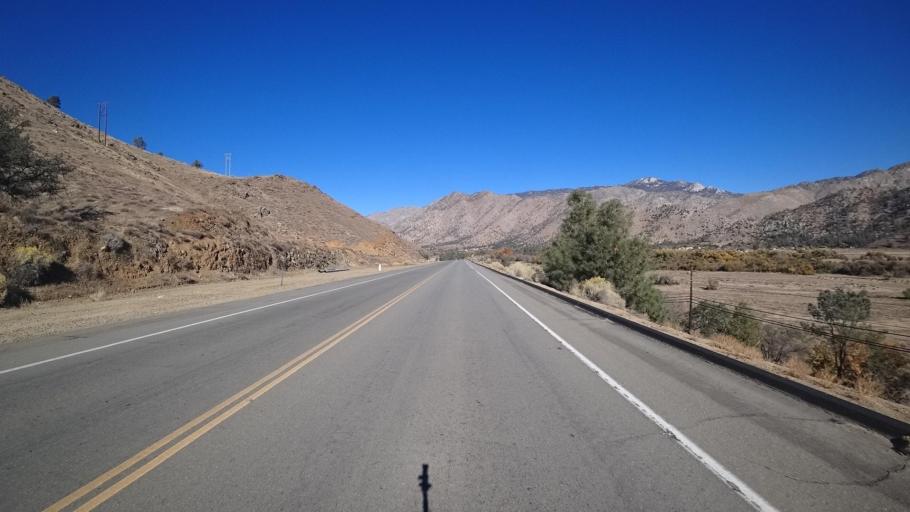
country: US
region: California
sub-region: Kern County
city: Kernville
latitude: 35.7308
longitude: -118.4291
